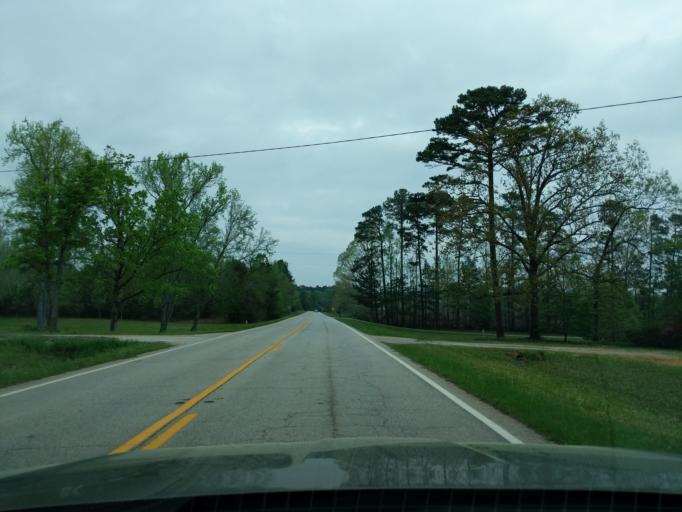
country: US
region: Georgia
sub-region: Lincoln County
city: Lincolnton
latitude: 33.7661
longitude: -82.3759
